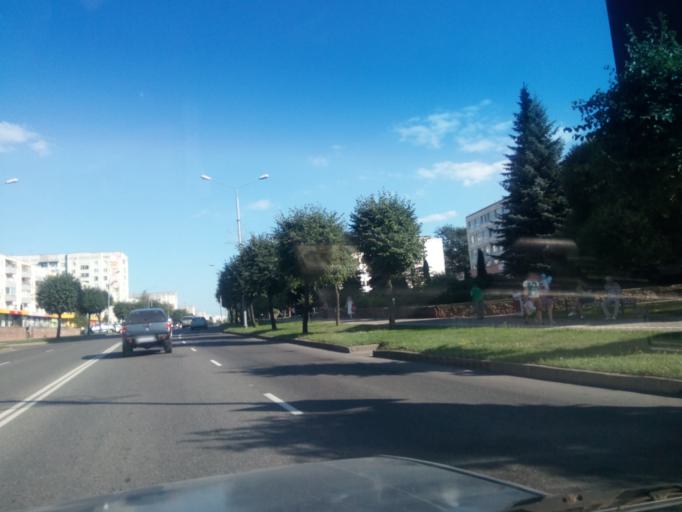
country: BY
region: Vitebsk
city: Navapolatsk
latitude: 55.5321
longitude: 28.6602
